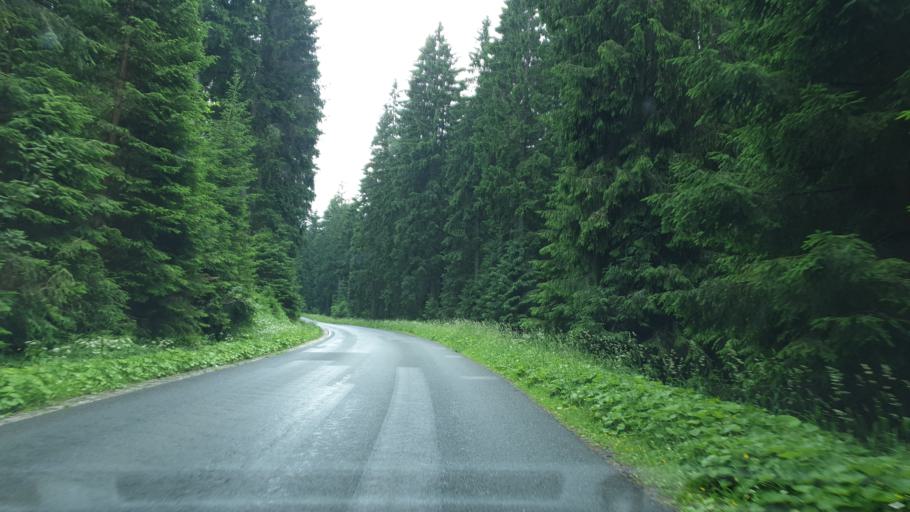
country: DE
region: Saxony
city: Tannenbergsthal
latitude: 50.4208
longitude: 12.4495
